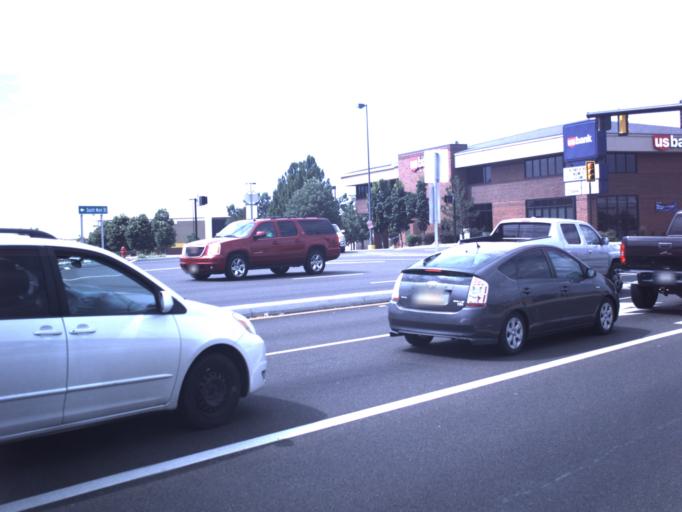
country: US
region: Utah
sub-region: Davis County
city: Layton
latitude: 41.0722
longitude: -111.9802
